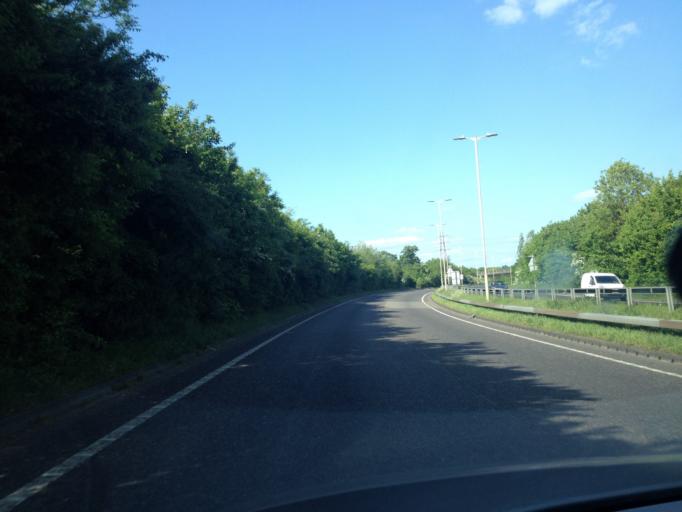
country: GB
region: England
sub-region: Hertfordshire
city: Watford
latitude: 51.6681
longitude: -0.3823
